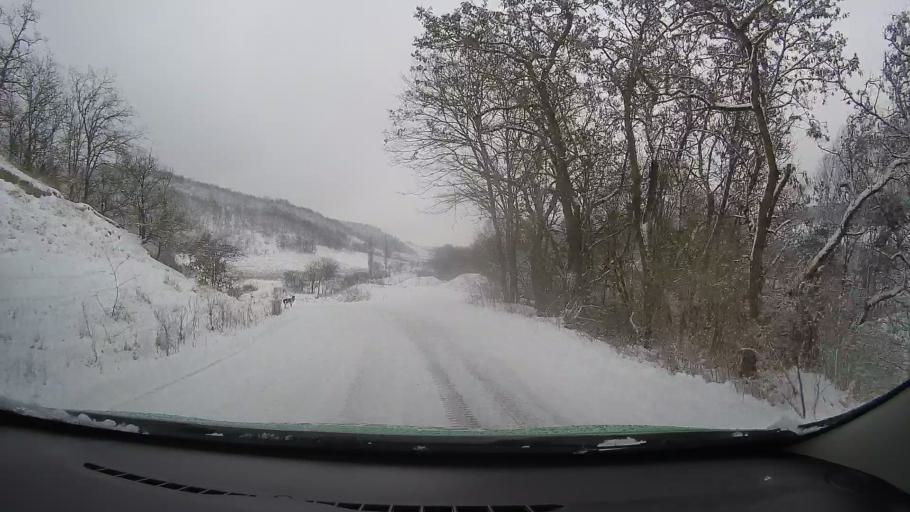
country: RO
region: Hunedoara
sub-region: Comuna Pestisu Mic
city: Pestisu Mic
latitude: 45.8232
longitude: 22.8639
